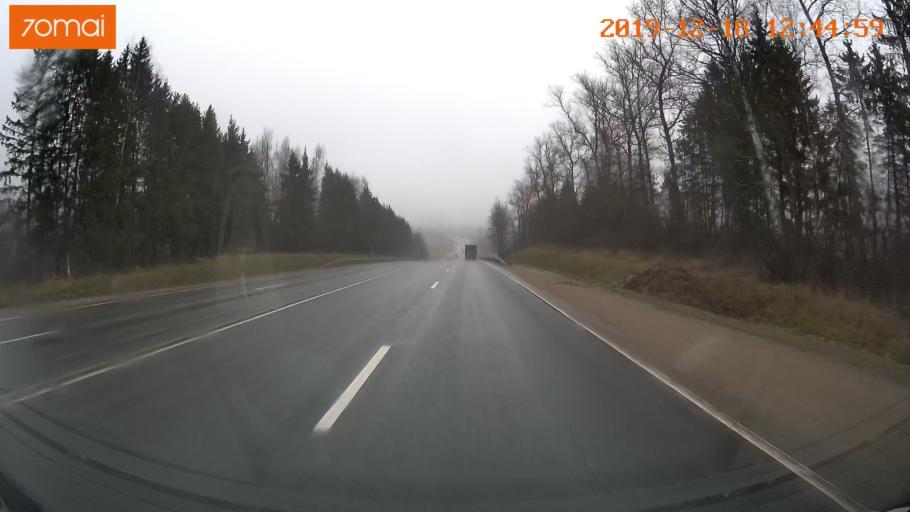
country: RU
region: Moskovskaya
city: Klin
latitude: 56.2262
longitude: 36.6533
